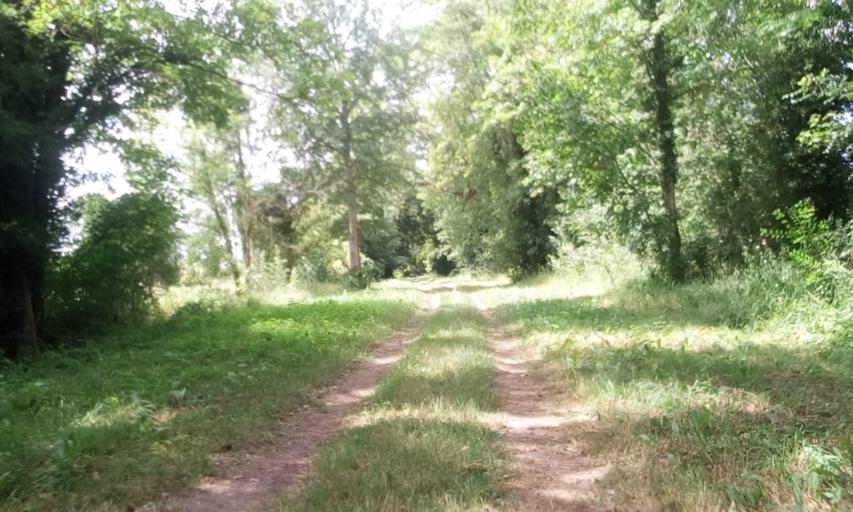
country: FR
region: Lower Normandy
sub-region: Departement du Calvados
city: Sannerville
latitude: 49.1585
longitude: -0.2094
